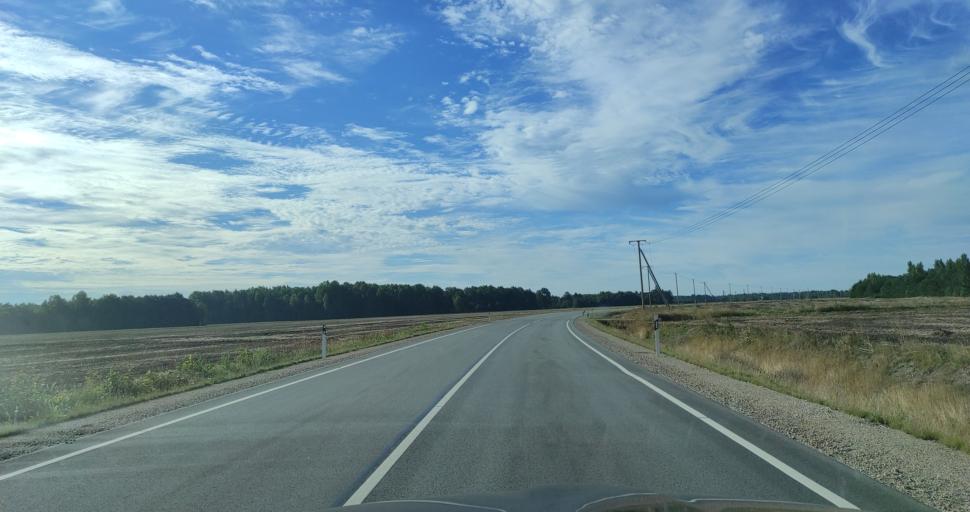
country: LV
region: Pavilostas
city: Pavilosta
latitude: 56.8293
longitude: 21.2242
